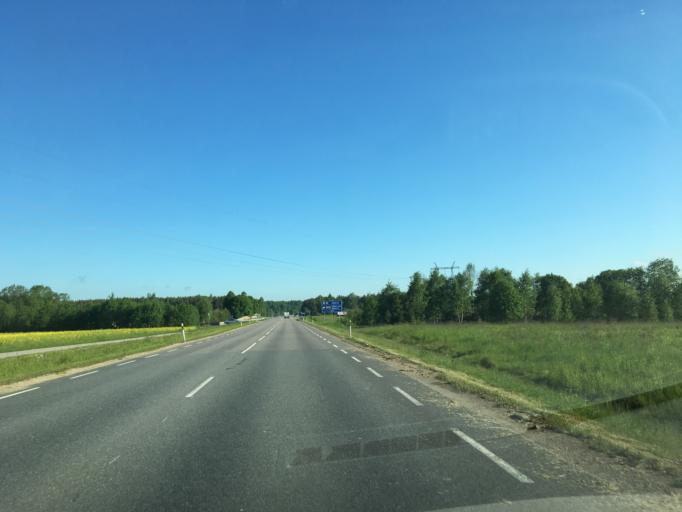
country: EE
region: Tartu
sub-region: Tartu linn
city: Tartu
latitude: 58.4512
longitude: 26.6752
